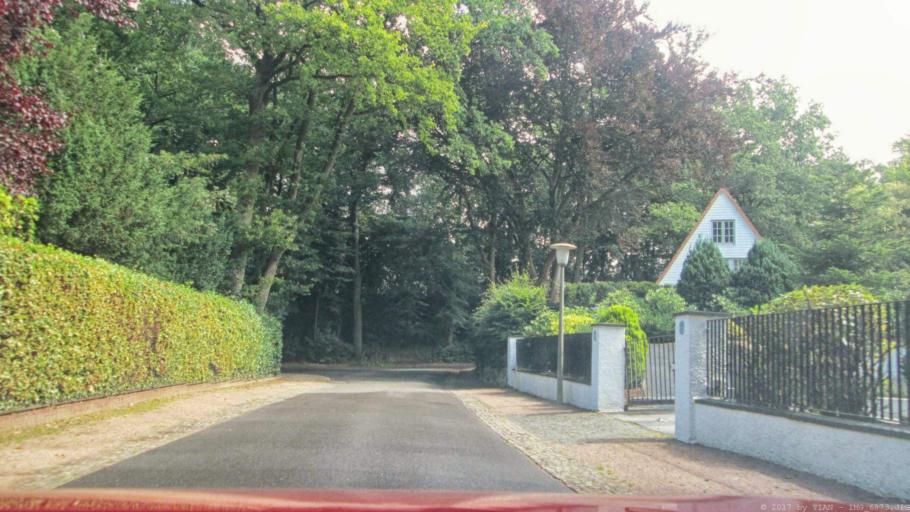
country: DE
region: Schleswig-Holstein
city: Halstenbek
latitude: 53.5708
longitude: 9.8037
